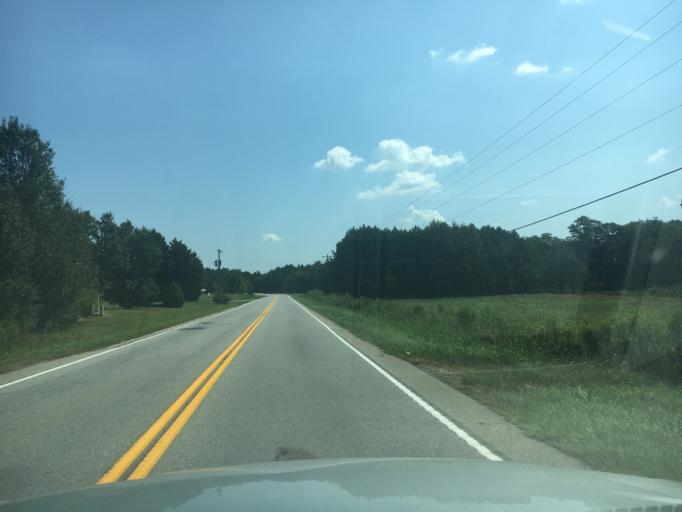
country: US
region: South Carolina
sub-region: Spartanburg County
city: Inman
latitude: 35.0846
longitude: -82.0522
